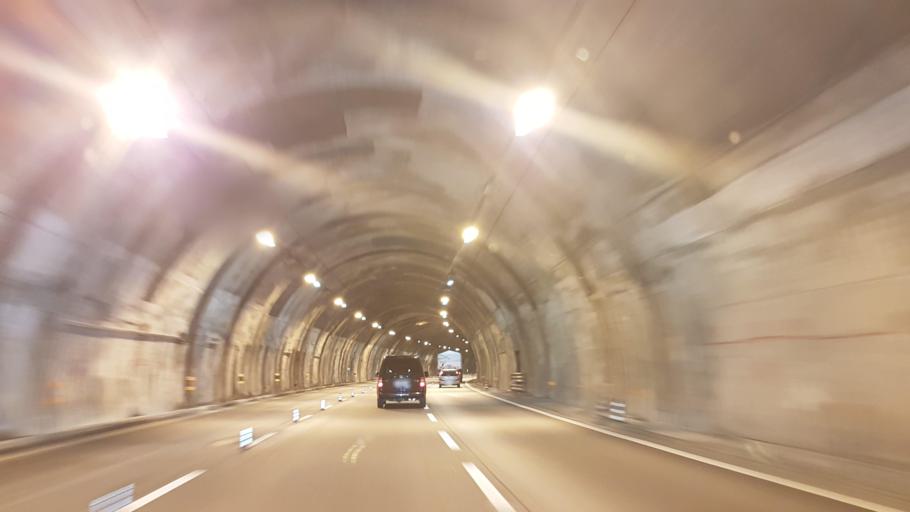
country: IT
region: Liguria
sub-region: Provincia di Genova
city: Masone
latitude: 44.4966
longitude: 8.7247
